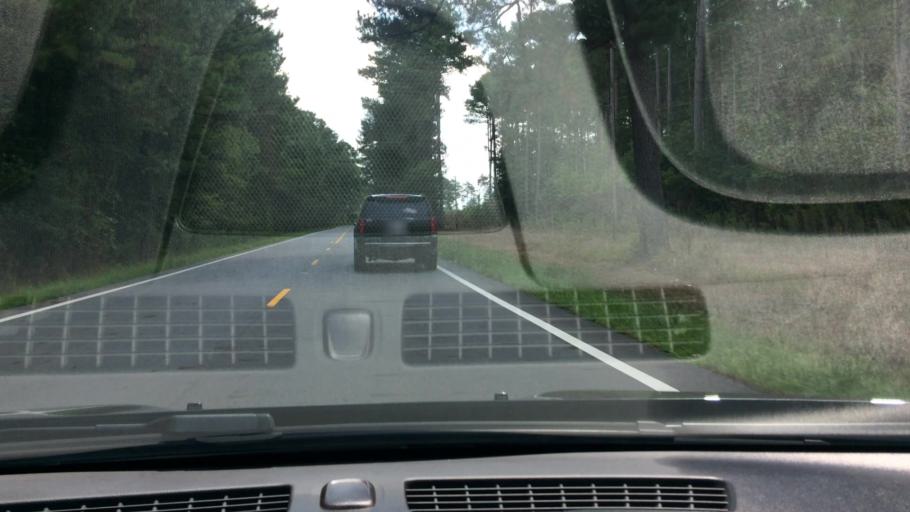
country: US
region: North Carolina
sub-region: Craven County
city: Vanceboro
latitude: 35.4284
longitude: -77.2076
